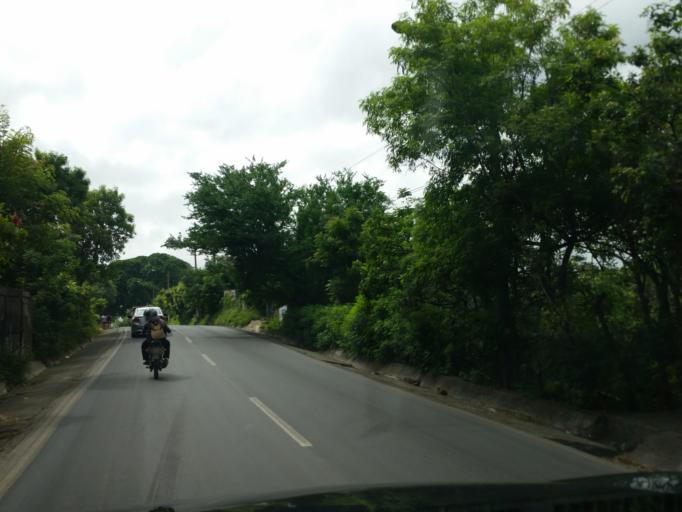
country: NI
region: Managua
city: Ciudad Sandino
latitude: 12.1038
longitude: -86.3241
